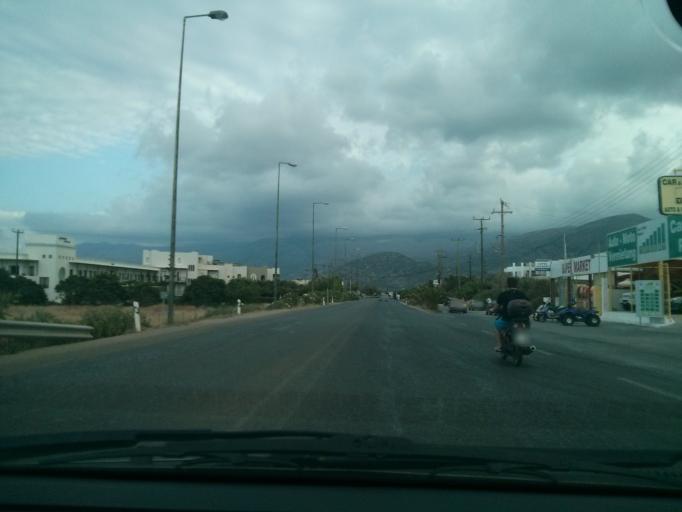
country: GR
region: Crete
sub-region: Nomos Irakleiou
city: Stalis
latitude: 35.3034
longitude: 25.4183
